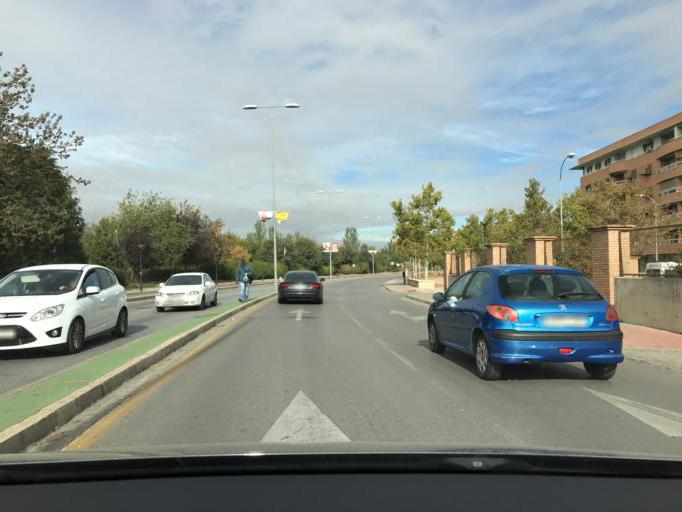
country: ES
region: Andalusia
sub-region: Provincia de Granada
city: Armilla
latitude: 37.1635
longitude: -3.6087
